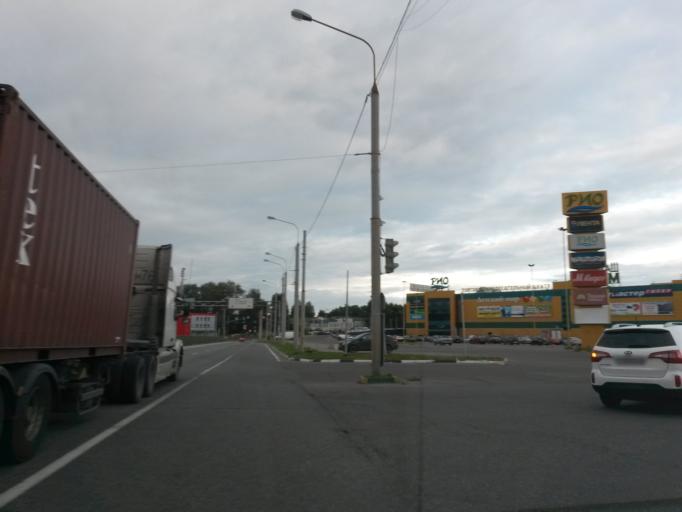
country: RU
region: Jaroslavl
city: Yaroslavl
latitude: 57.6720
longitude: 39.8342
